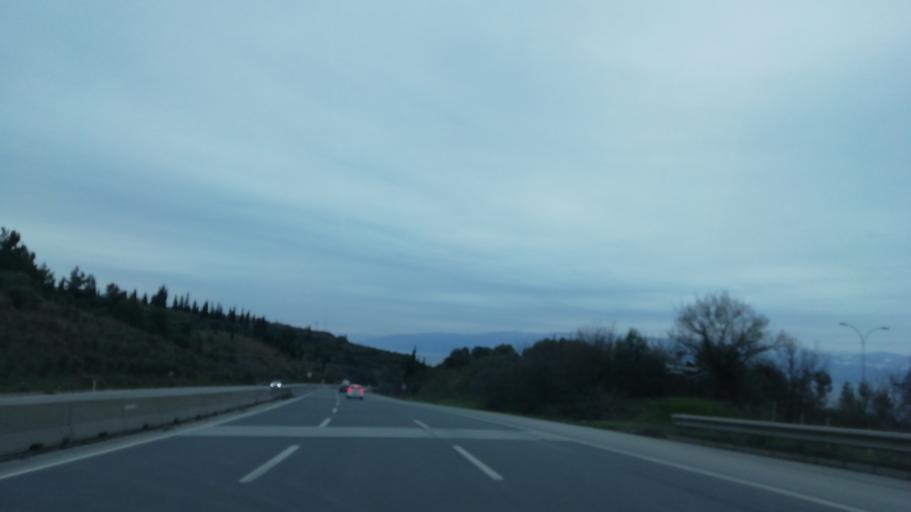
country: TR
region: Kocaeli
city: Tavsancil
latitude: 40.7737
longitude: 29.5571
